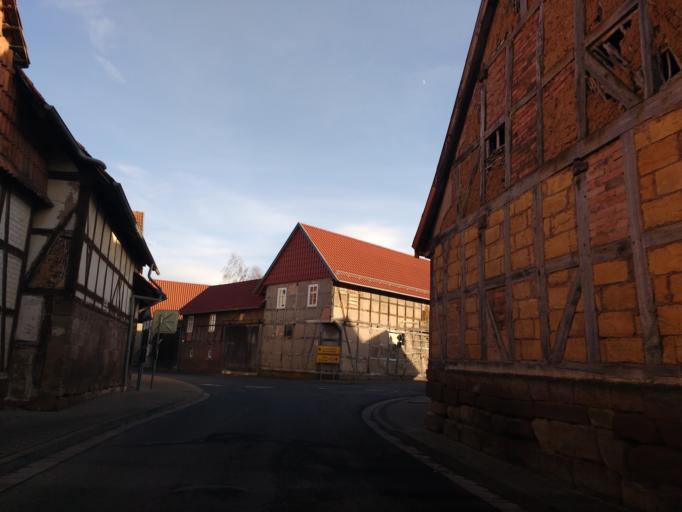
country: DE
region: Thuringia
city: Burgwalde
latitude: 51.3888
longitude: 10.0435
